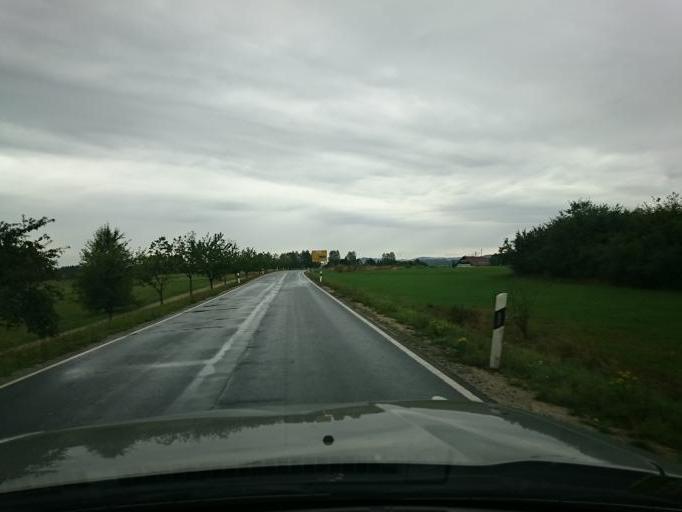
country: DE
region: Bavaria
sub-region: Upper Franconia
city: Pottenstein
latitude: 49.7588
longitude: 11.4029
